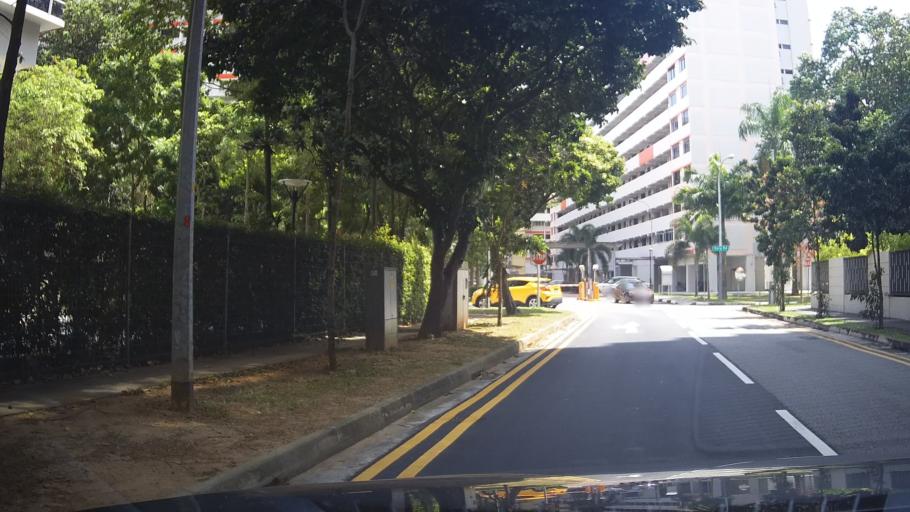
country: SG
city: Singapore
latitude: 1.3121
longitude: 103.8961
